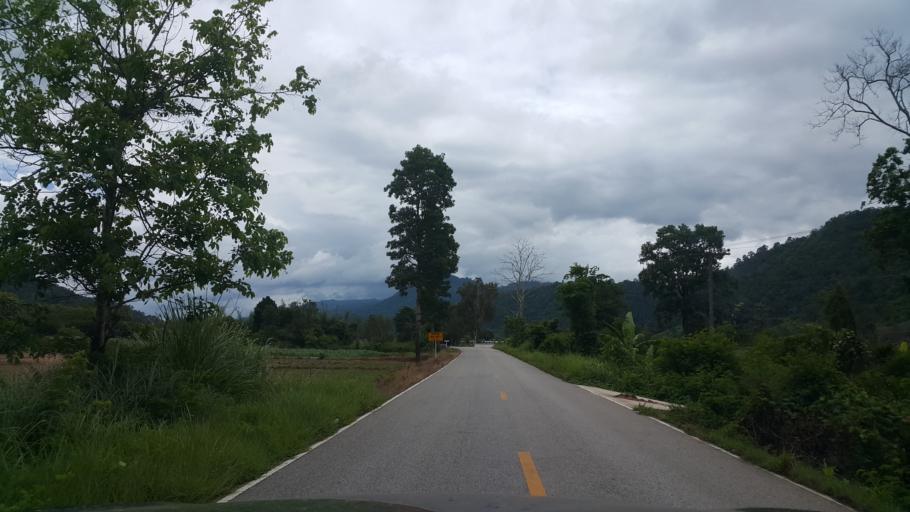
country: TH
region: Phitsanulok
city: Chat Trakan
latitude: 17.3770
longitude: 100.7484
